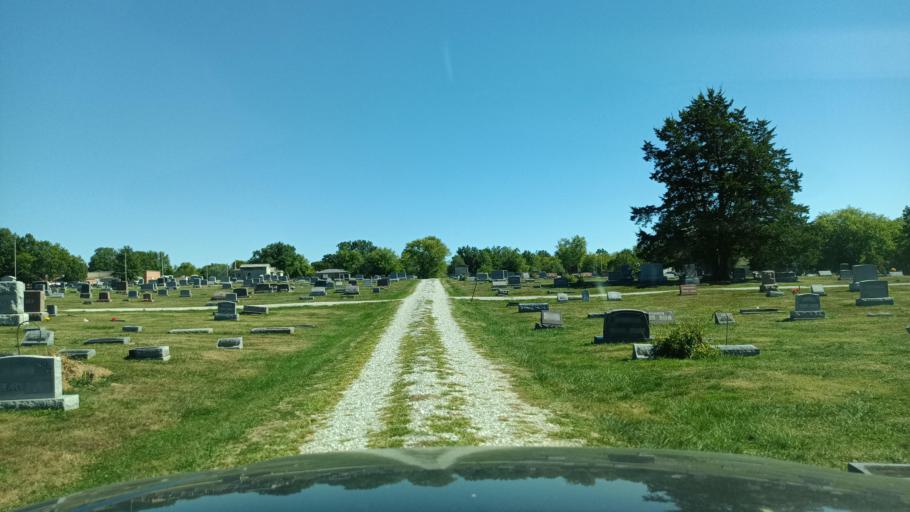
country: US
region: Missouri
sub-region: Macon County
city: La Plata
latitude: 40.0217
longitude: -92.4995
